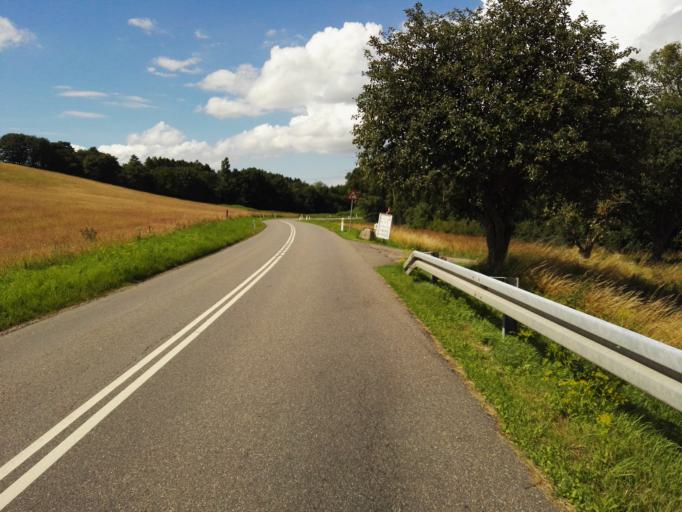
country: DK
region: Capital Region
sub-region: Egedal Kommune
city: Vekso
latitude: 55.7626
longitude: 12.2296
